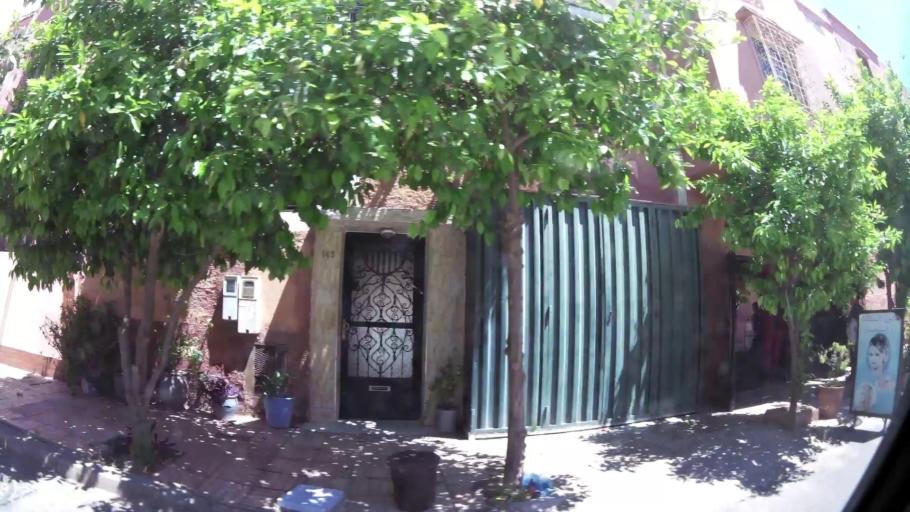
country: MA
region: Marrakech-Tensift-Al Haouz
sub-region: Marrakech
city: Marrakesh
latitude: 31.6519
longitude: -7.9986
